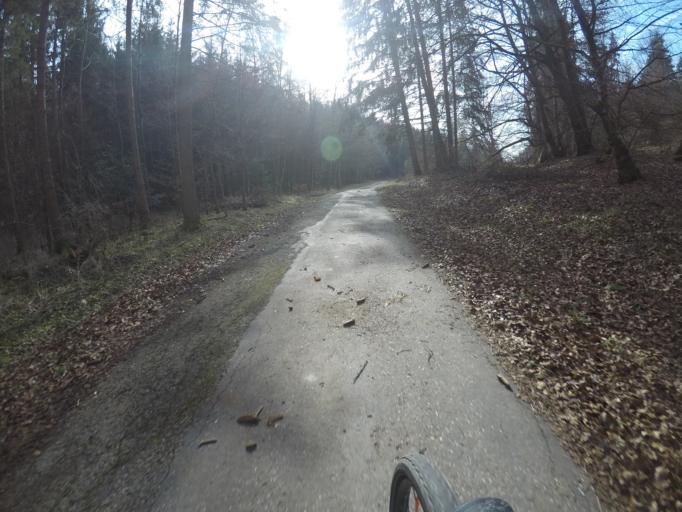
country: DE
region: Baden-Wuerttemberg
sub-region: Regierungsbezirk Stuttgart
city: Deckenpfronn
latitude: 48.6705
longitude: 8.7747
